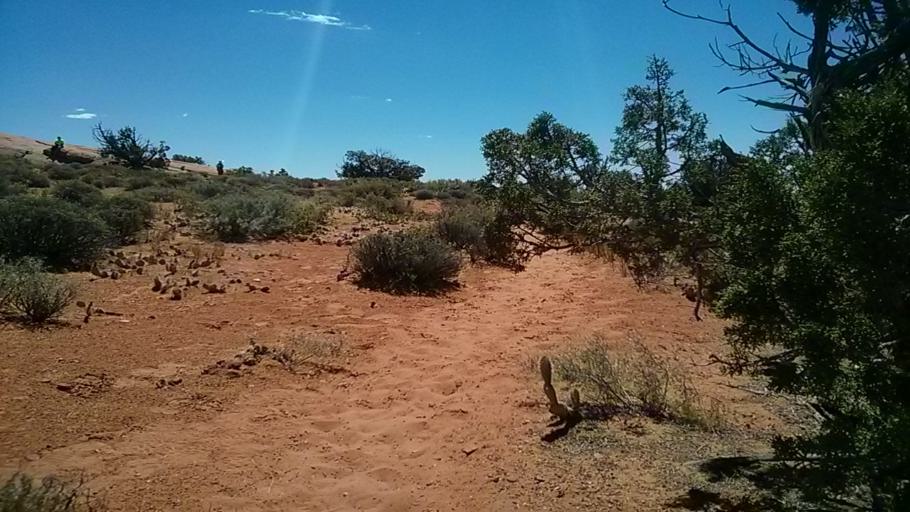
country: US
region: Arizona
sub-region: Coconino County
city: Page
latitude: 37.4855
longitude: -111.2157
